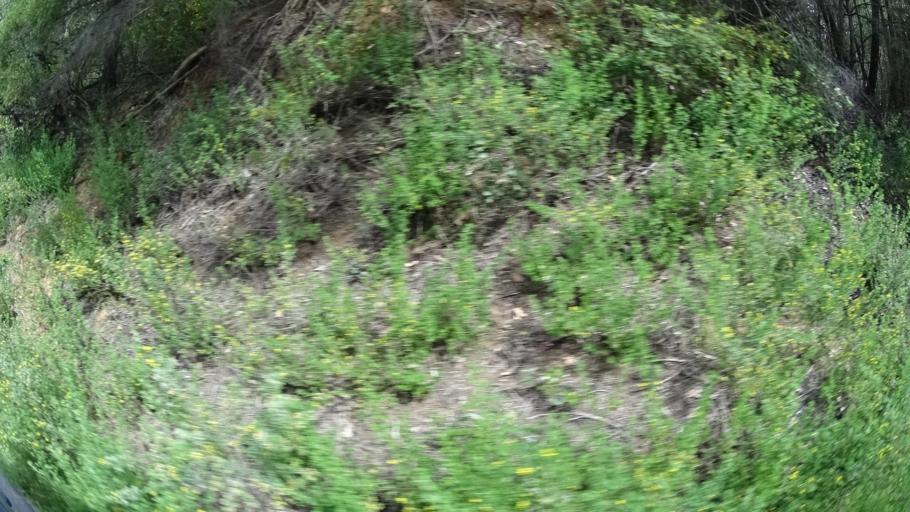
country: US
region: California
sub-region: Humboldt County
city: Redway
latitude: 40.1480
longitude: -123.6284
